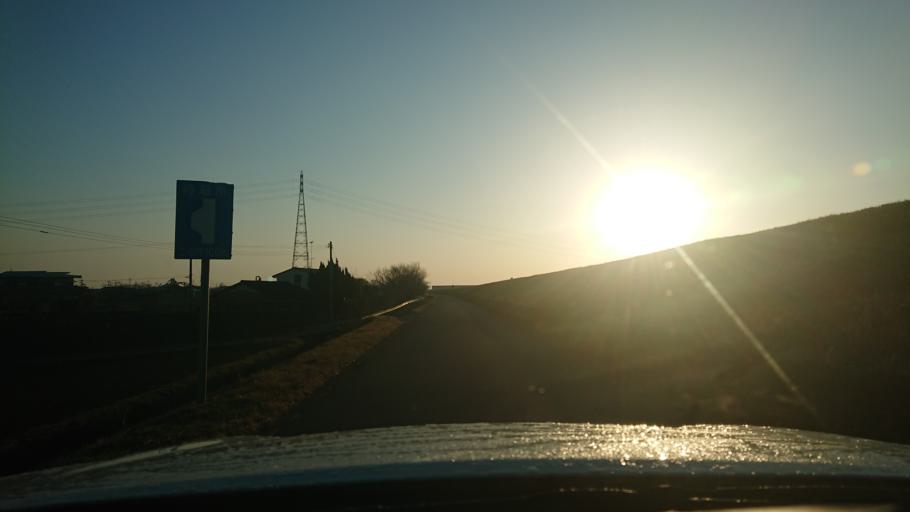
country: JP
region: Tokushima
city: Anan
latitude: 33.9407
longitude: 134.6018
